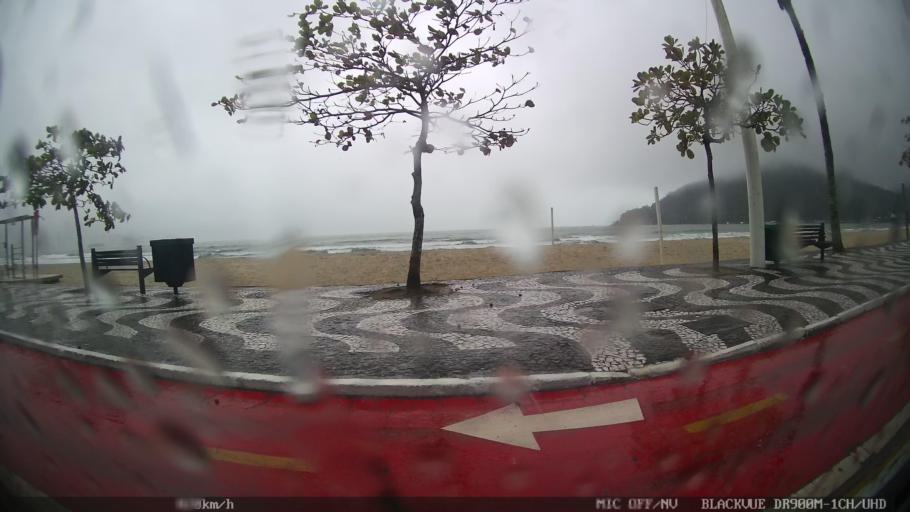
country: BR
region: Santa Catarina
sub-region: Balneario Camboriu
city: Balneario Camboriu
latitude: -27.0054
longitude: -48.6132
